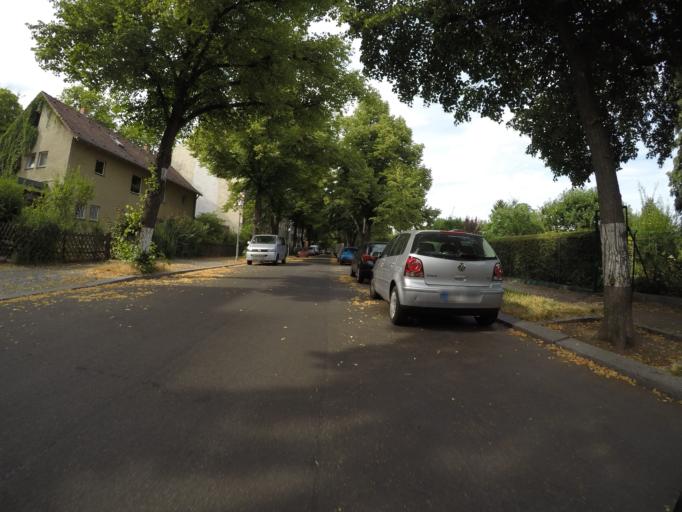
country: DE
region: Berlin
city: Wilmersdorf Bezirk
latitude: 52.4750
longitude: 13.3110
